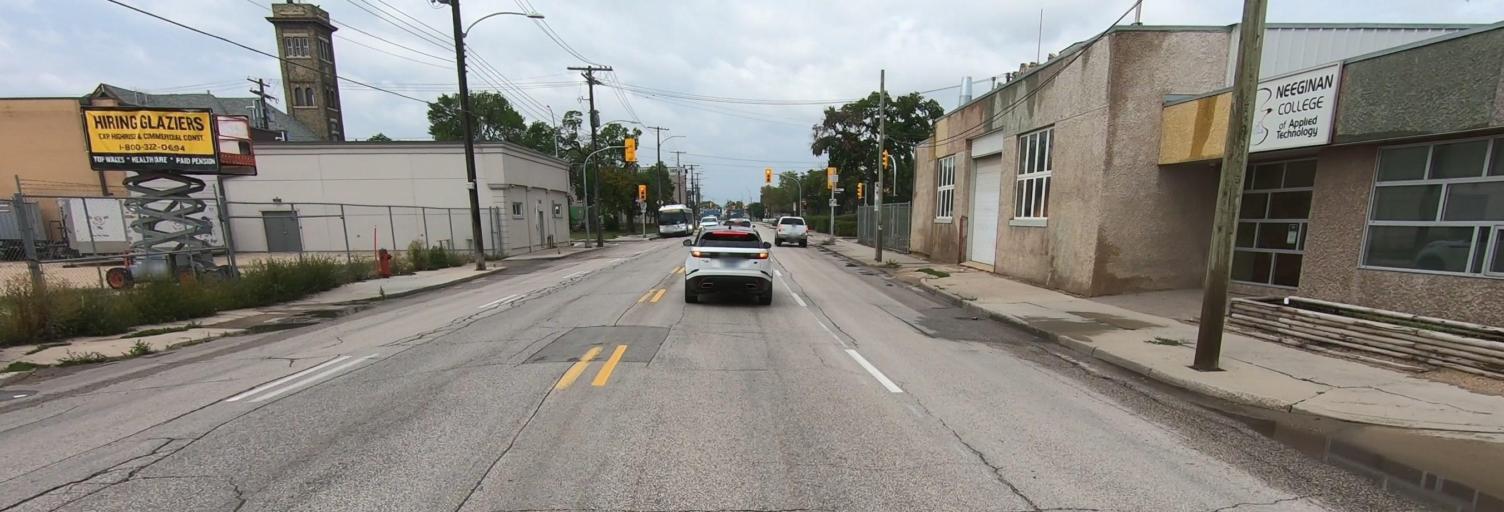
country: CA
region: Manitoba
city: Winnipeg
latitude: 49.9040
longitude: -97.1304
